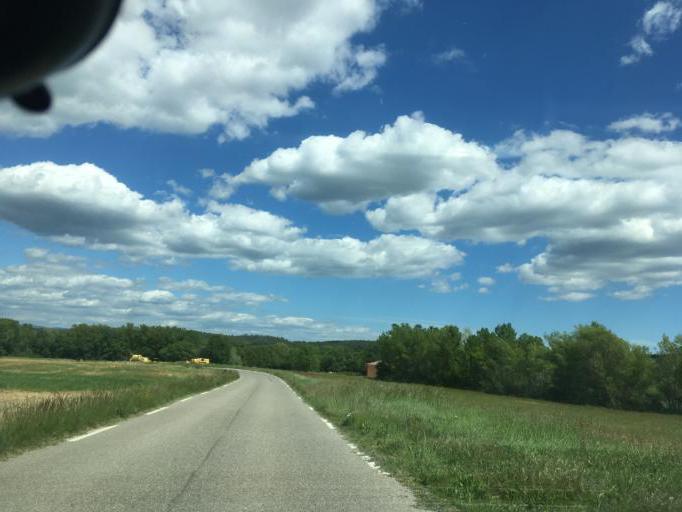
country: FR
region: Provence-Alpes-Cote d'Azur
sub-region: Departement du Var
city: Ginasservis
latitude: 43.5952
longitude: 5.8993
